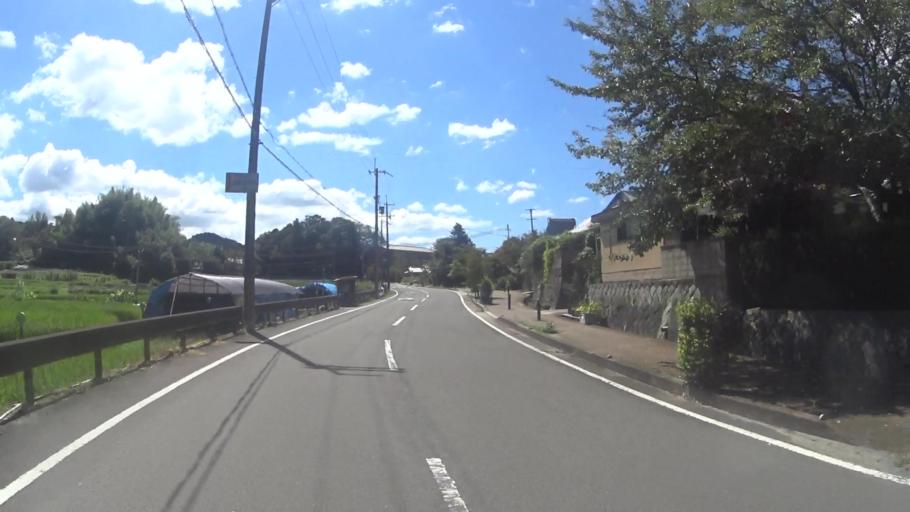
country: JP
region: Nara
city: Nara-shi
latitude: 34.7664
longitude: 135.8799
